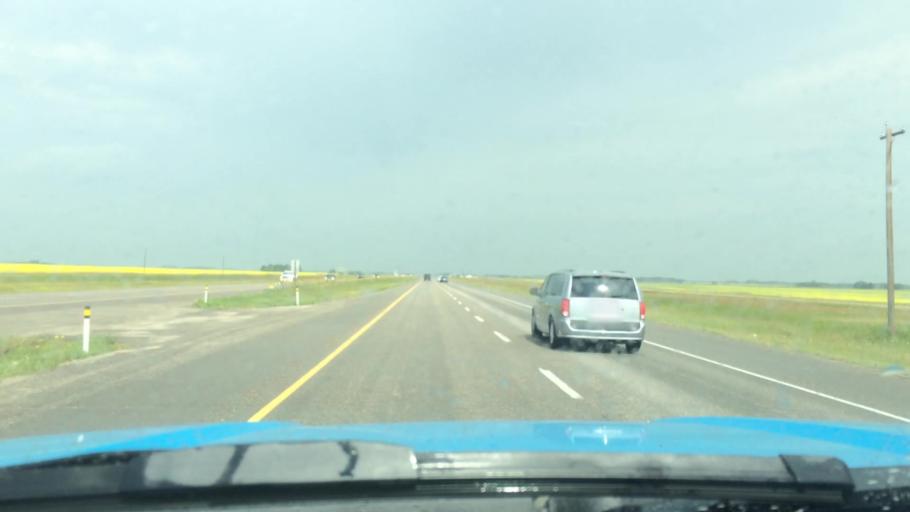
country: CA
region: Alberta
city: Didsbury
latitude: 51.6780
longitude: -114.0253
